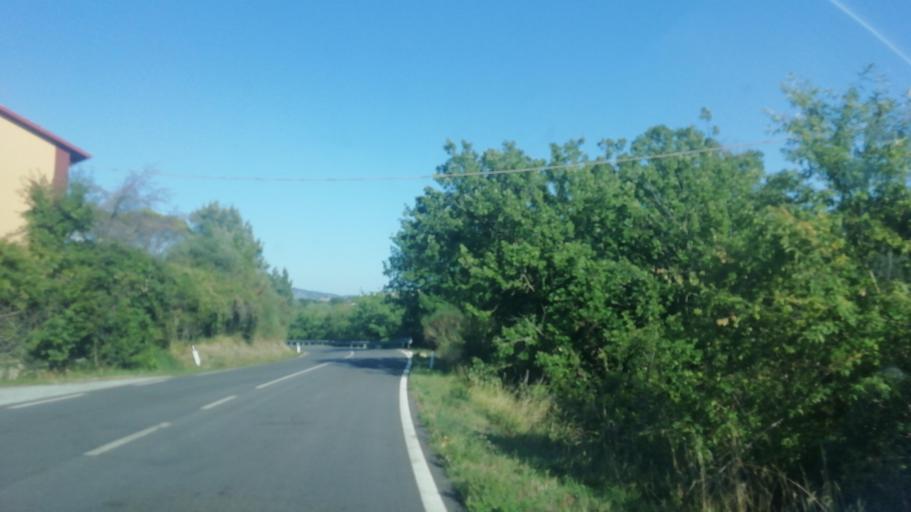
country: IT
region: The Marches
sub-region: Provincia di Pesaro e Urbino
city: Frontone
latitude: 43.5430
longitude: 12.7645
